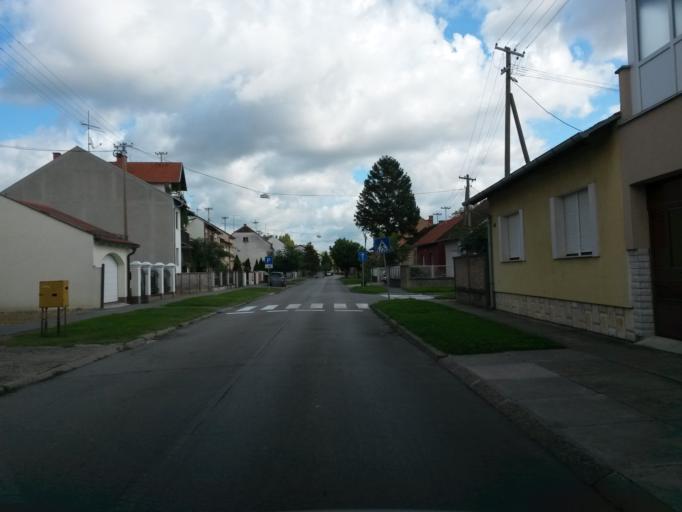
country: HR
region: Osjecko-Baranjska
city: Visnjevac
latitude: 45.5610
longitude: 18.6488
